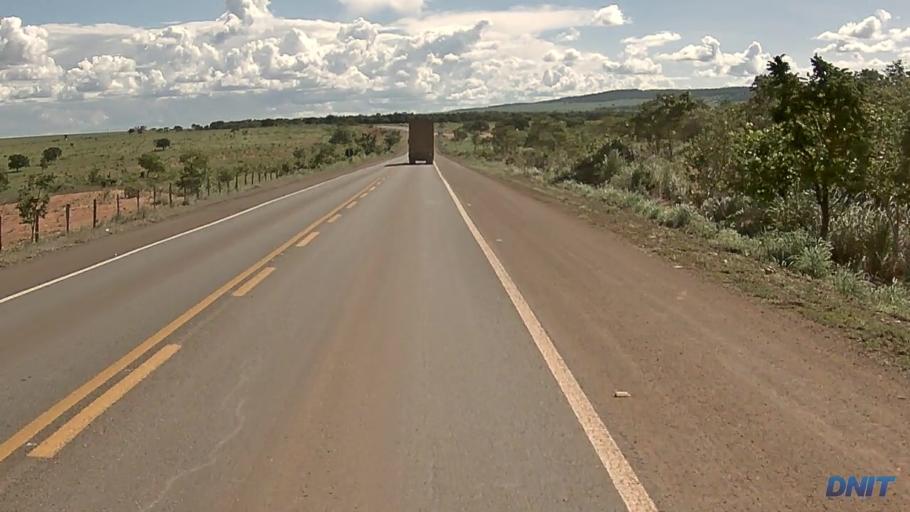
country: BR
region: Goias
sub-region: Padre Bernardo
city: Padre Bernardo
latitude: -15.1524
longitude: -48.3503
